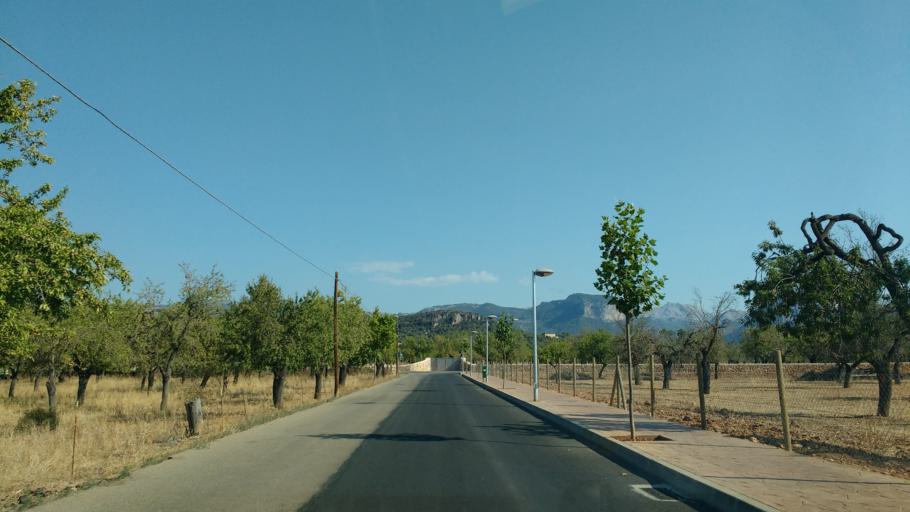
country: ES
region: Balearic Islands
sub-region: Illes Balears
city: Consell
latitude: 39.6731
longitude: 2.8102
